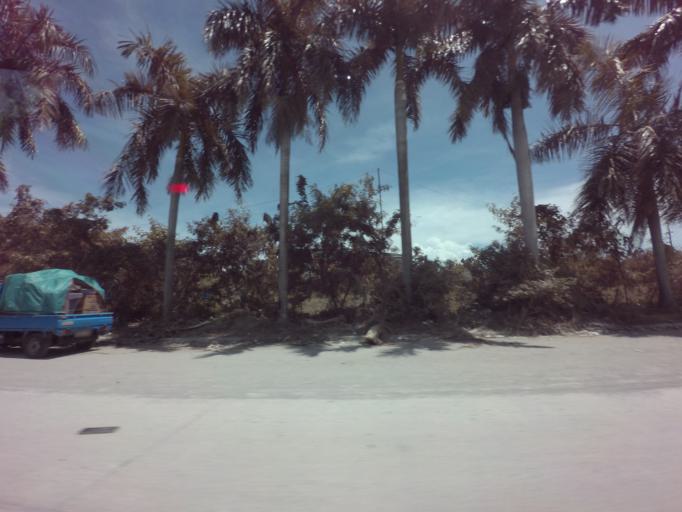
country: PH
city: Sambayanihan People's Village
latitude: 14.5093
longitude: 120.9805
